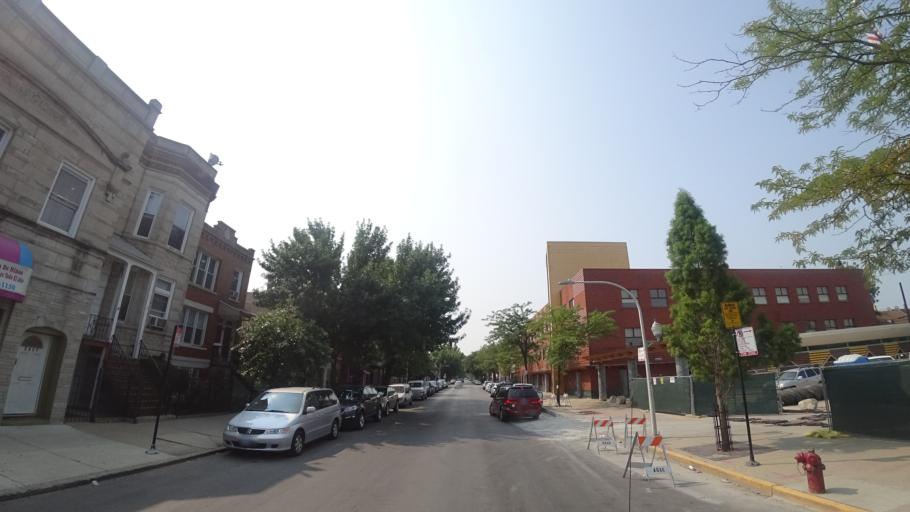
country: US
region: Illinois
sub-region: Cook County
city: Cicero
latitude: 41.8436
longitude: -87.7172
